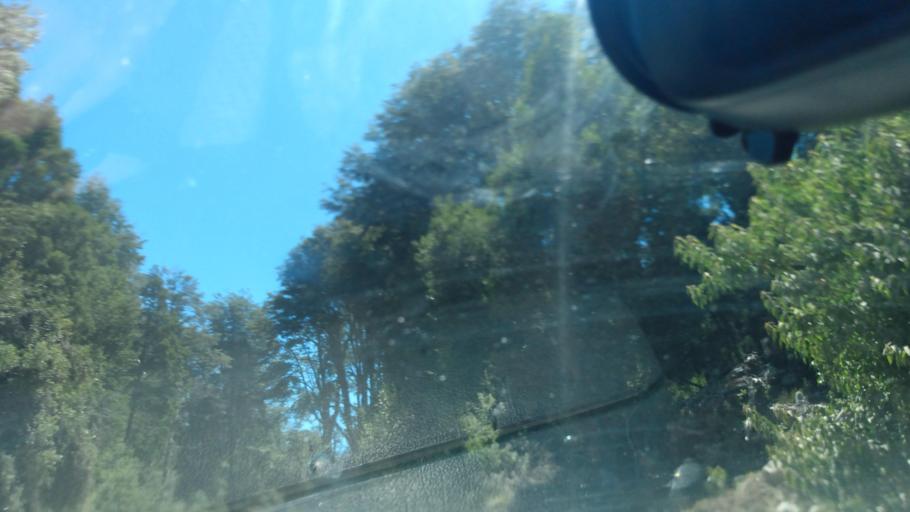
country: AR
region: Neuquen
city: Villa La Angostura
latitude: -40.6167
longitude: -71.5330
